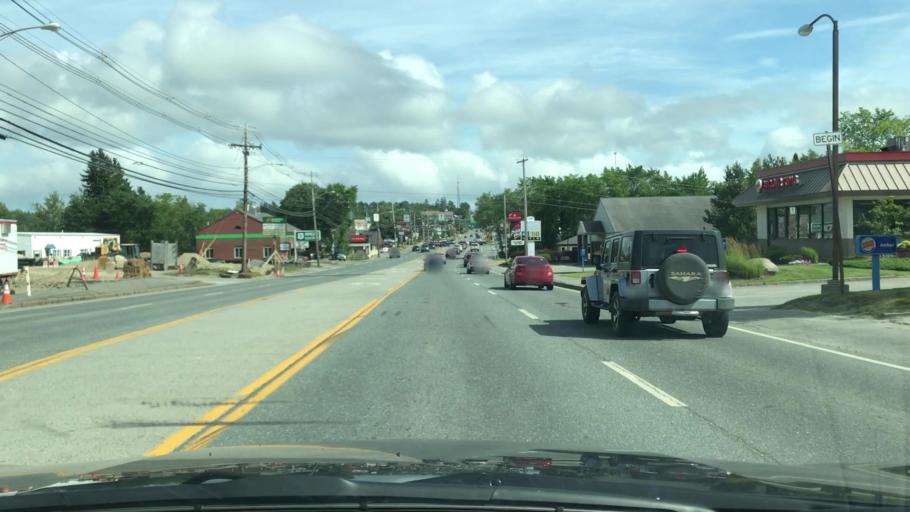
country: US
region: Maine
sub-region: Hancock County
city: Ellsworth
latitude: 44.5347
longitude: -68.4105
